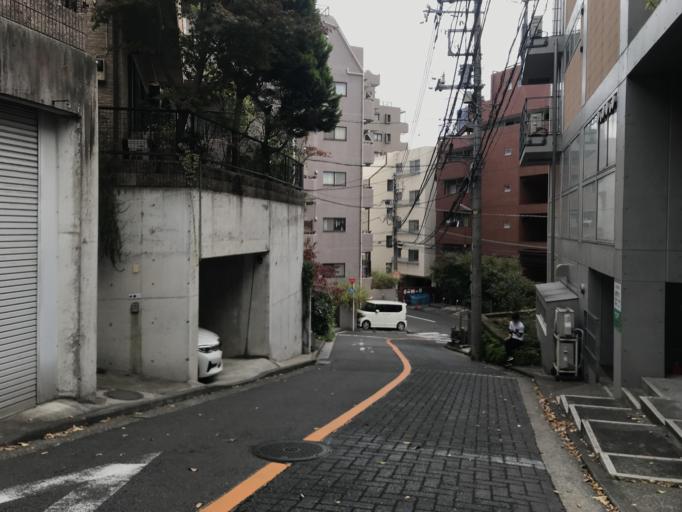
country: JP
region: Kanagawa
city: Yokohama
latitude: 35.4704
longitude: 139.6218
